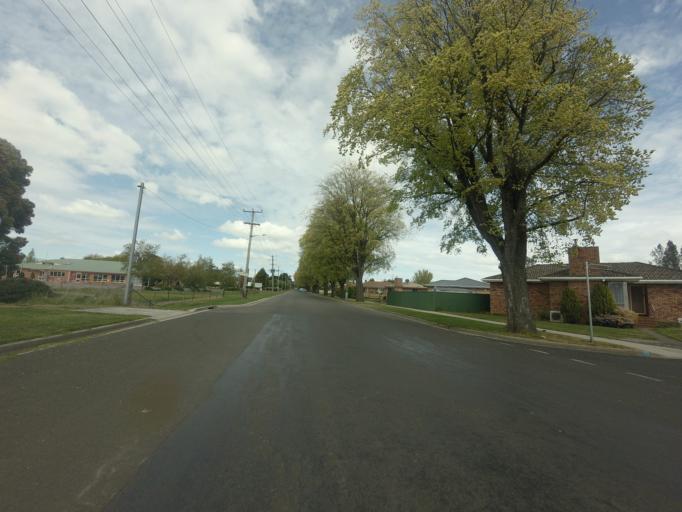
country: AU
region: Tasmania
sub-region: Northern Midlands
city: Longford
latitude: -41.6033
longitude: 147.1253
